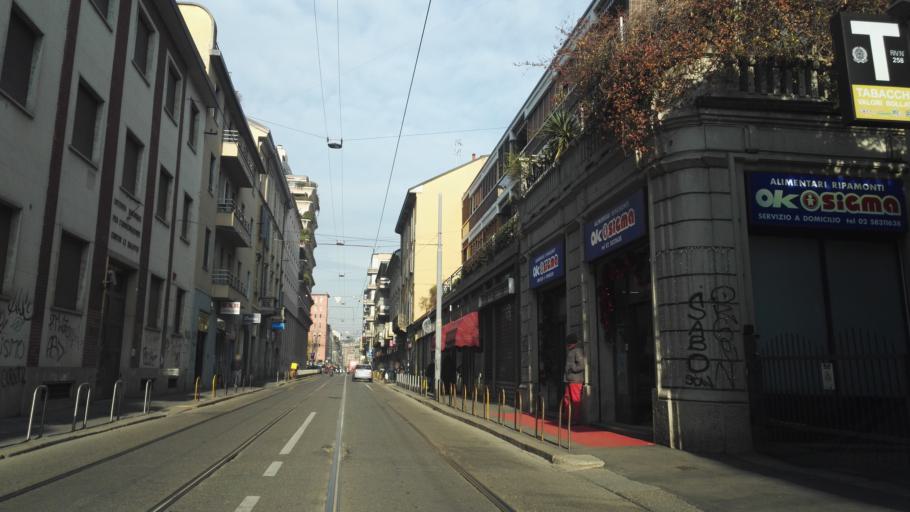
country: IT
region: Lombardy
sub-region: Citta metropolitana di Milano
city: Milano
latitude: 45.4496
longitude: 9.1972
